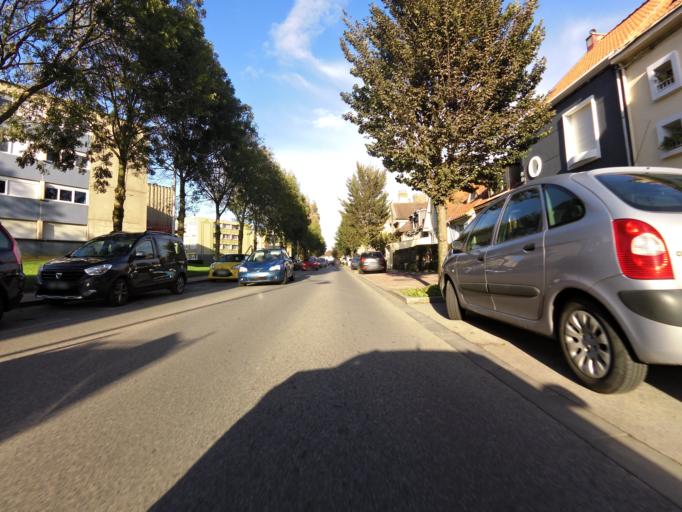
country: FR
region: Nord-Pas-de-Calais
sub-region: Departement du Pas-de-Calais
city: Saint-Martin-Boulogne
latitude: 50.7374
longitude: 1.6147
